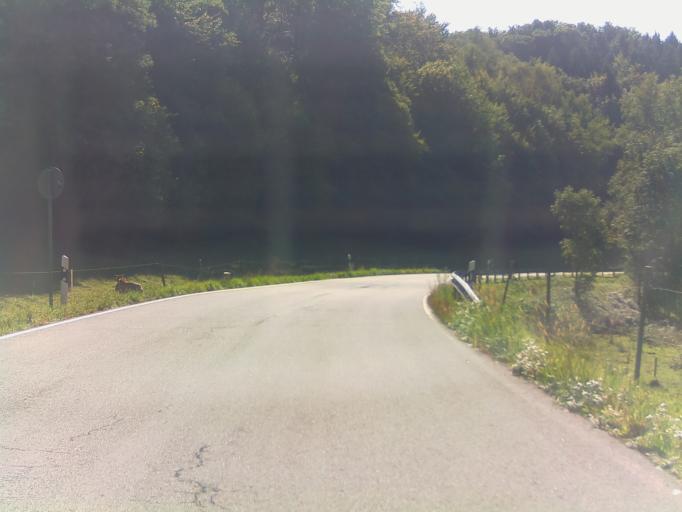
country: DE
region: Hesse
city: Unter-Abtsteinach
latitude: 49.5034
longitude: 8.7712
